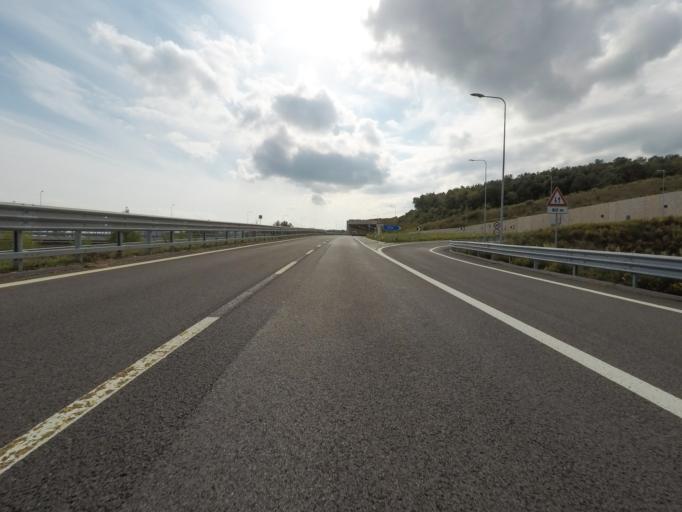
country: IT
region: Tuscany
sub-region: Provincia di Grosseto
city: Civitella Marittima
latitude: 43.0979
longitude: 11.2992
